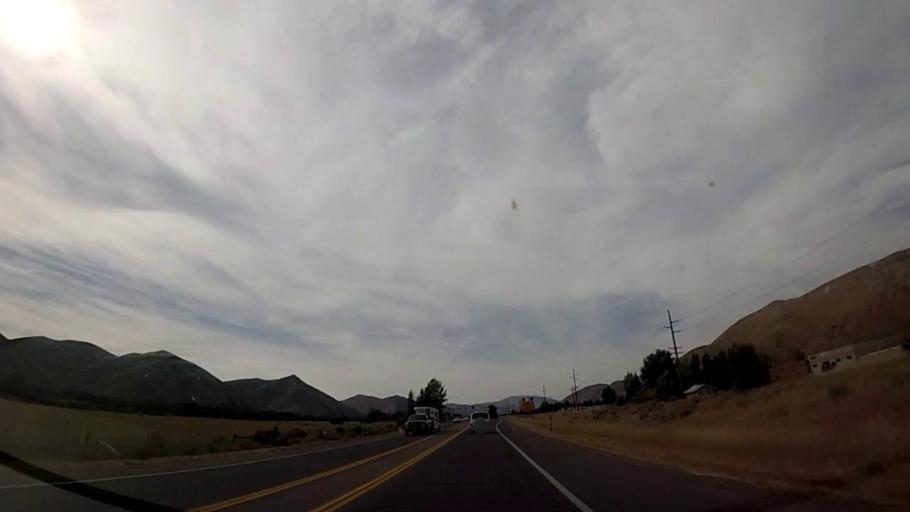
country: US
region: Idaho
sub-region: Blaine County
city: Bellevue
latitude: 43.4846
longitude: -114.2752
